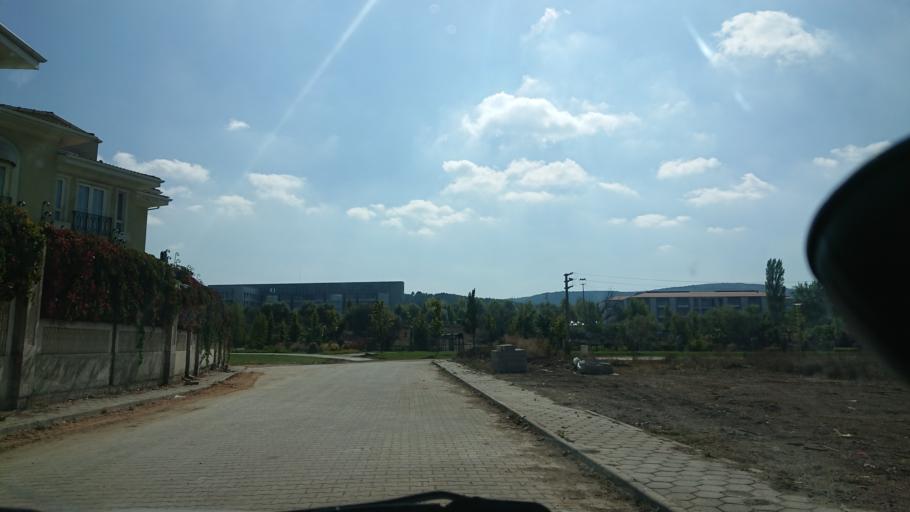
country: TR
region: Eskisehir
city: Eskisehir
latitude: 39.7545
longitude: 30.4784
